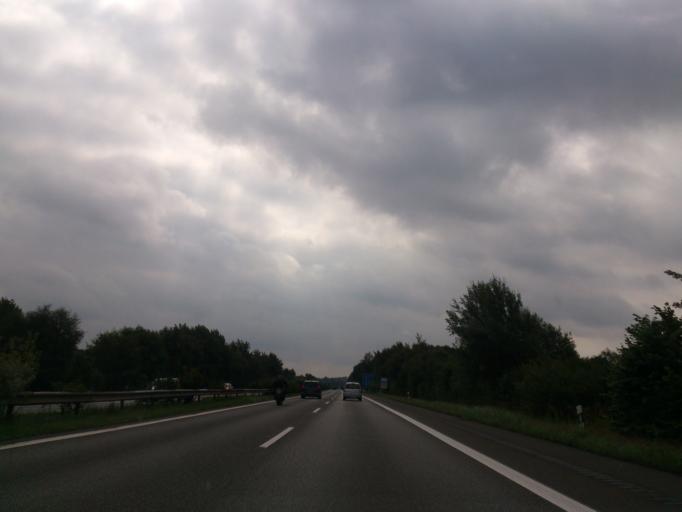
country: DE
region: Schleswig-Holstein
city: Seeth-Ekholt
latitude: 53.7232
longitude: 9.7394
